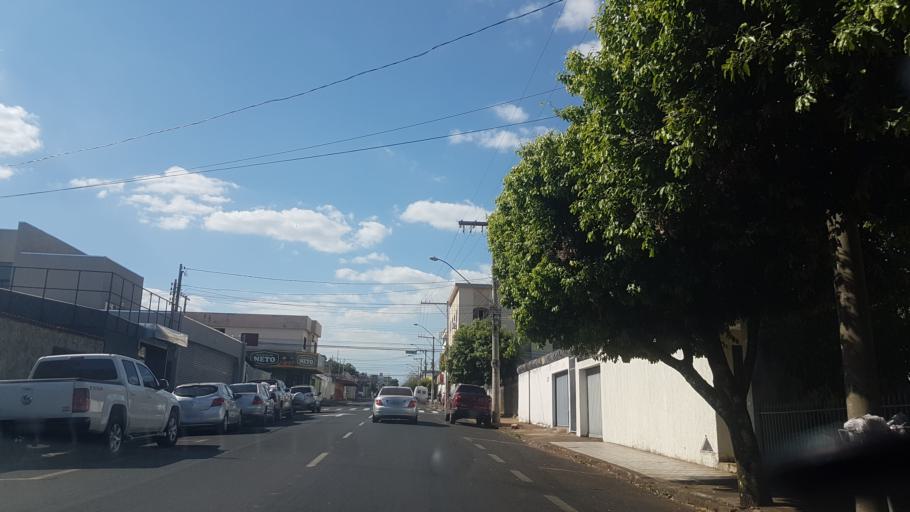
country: BR
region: Minas Gerais
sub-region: Uberlandia
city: Uberlandia
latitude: -18.8968
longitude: -48.2685
